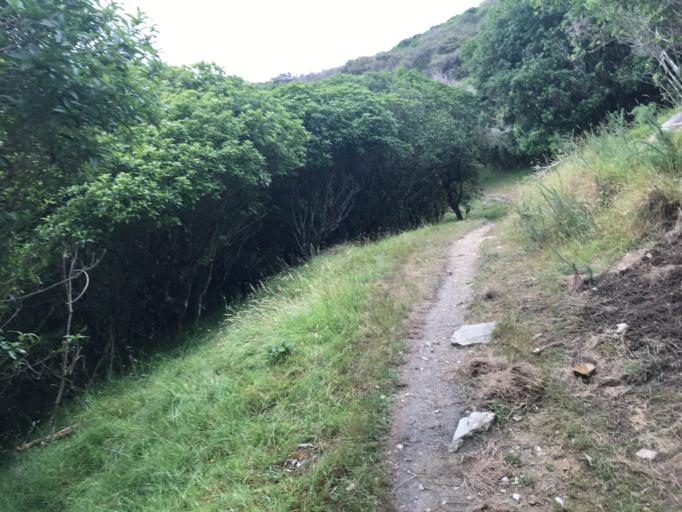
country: NZ
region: Marlborough
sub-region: Marlborough District
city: Picton
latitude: -41.2339
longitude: 173.9581
